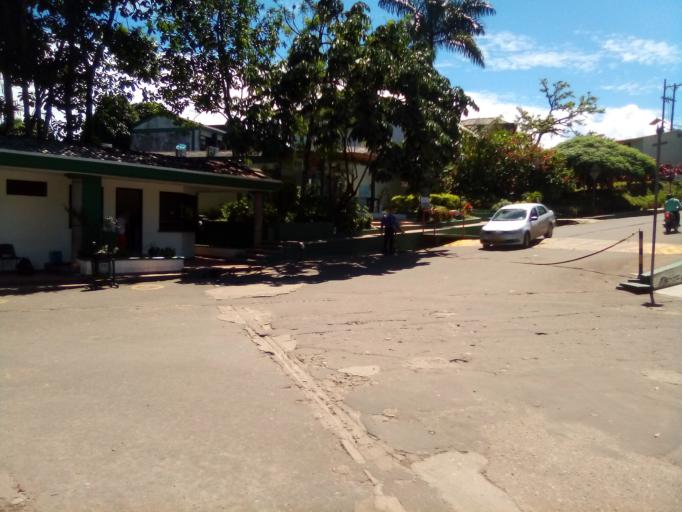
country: CO
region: Caqueta
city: Florencia
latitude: 1.6202
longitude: -75.6052
